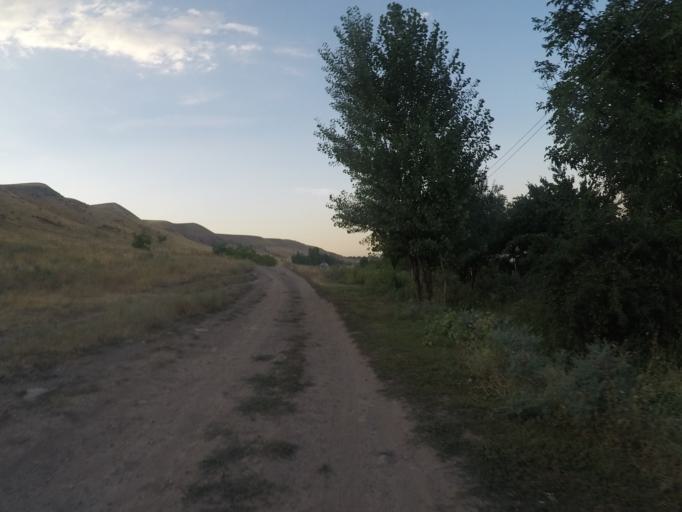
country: KG
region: Chuy
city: Bishkek
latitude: 42.7691
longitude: 74.6388
